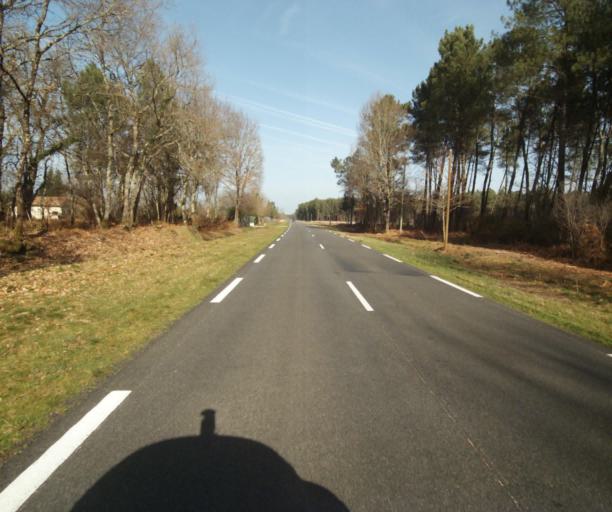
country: FR
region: Aquitaine
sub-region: Departement de la Gironde
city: Grignols
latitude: 44.1979
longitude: -0.1393
